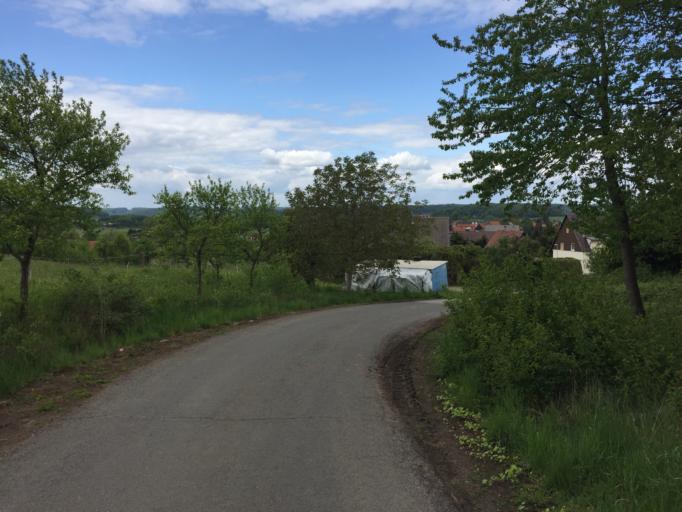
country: DE
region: Hesse
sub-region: Regierungsbezirk Giessen
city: Reiskirchen
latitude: 50.5744
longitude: 8.8186
